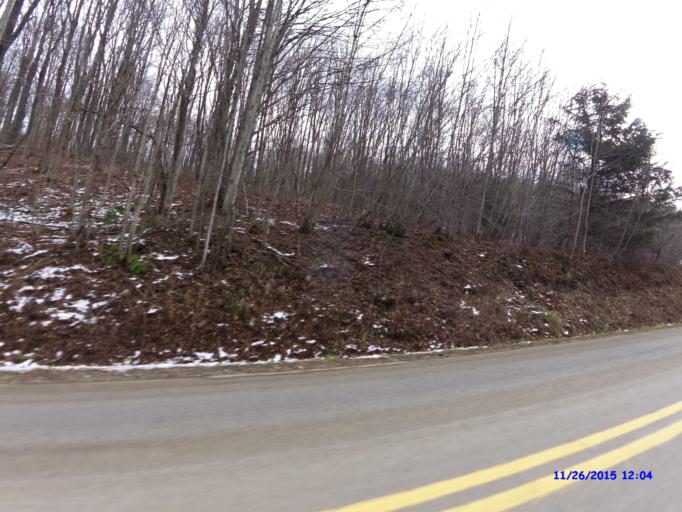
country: US
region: New York
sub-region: Cattaraugus County
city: Franklinville
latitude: 42.2416
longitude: -78.4348
